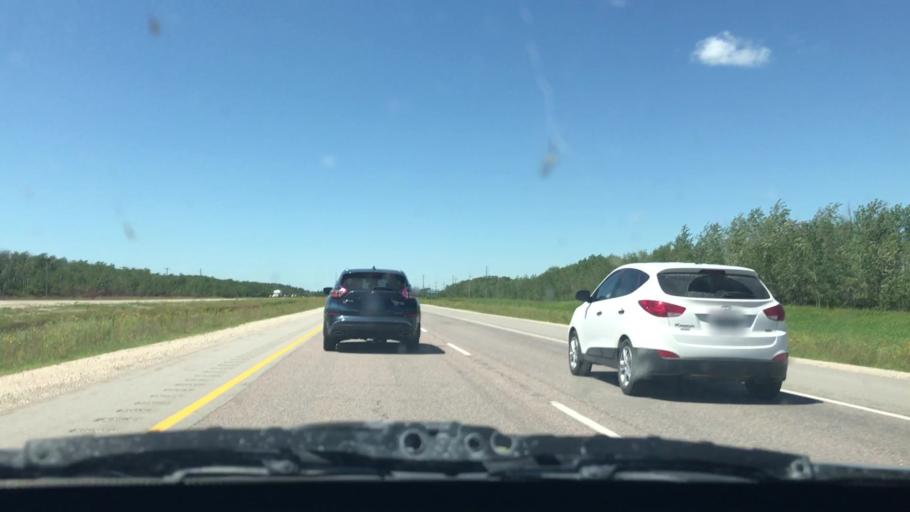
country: CA
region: Manitoba
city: La Broquerie
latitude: 49.6756
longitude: -96.5818
